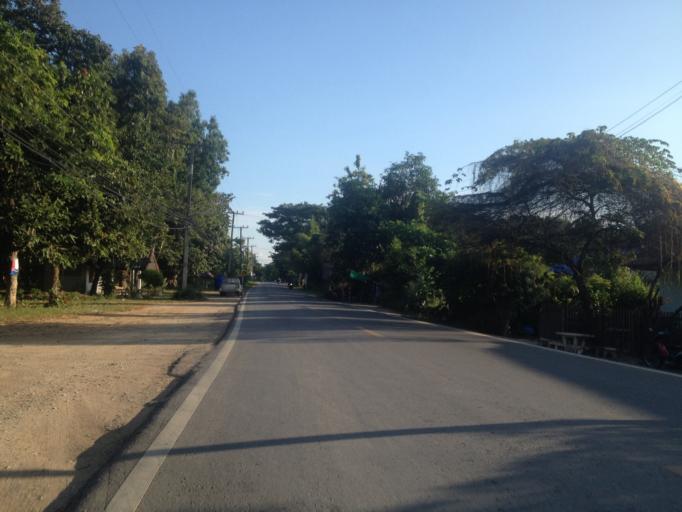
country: TH
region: Chiang Mai
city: San Pa Tong
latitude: 18.5752
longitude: 98.8666
